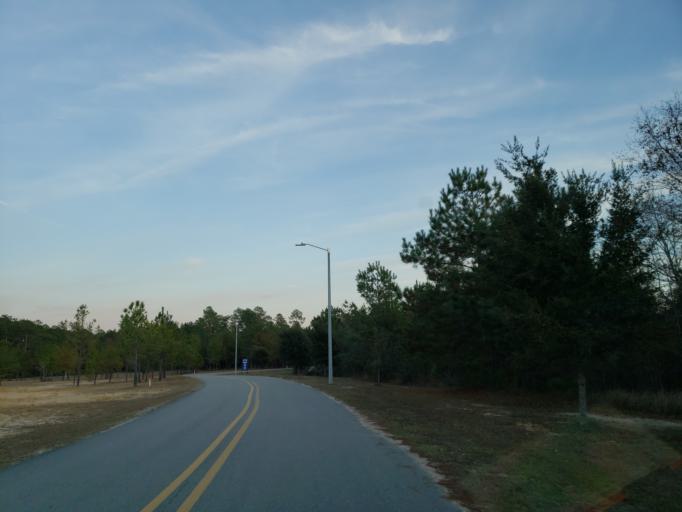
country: US
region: Mississippi
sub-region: Forrest County
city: Hattiesburg
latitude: 31.2795
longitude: -89.3145
